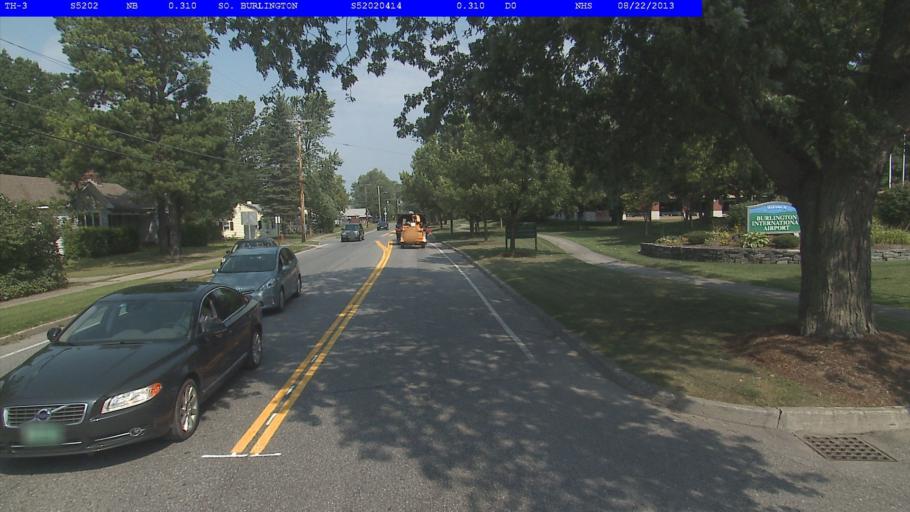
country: US
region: Vermont
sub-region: Chittenden County
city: South Burlington
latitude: 44.4673
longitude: -73.1559
